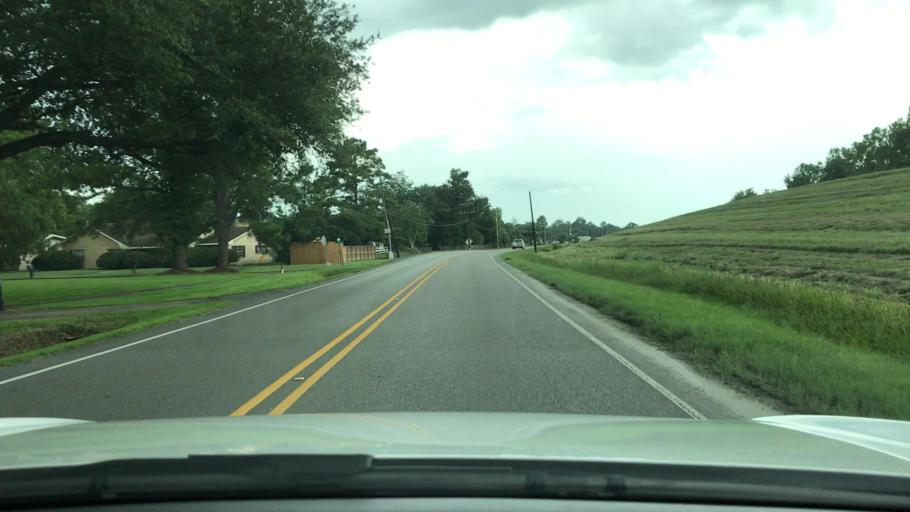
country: US
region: Louisiana
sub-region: Iberville Parish
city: Plaquemine
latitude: 30.2770
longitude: -91.2139
